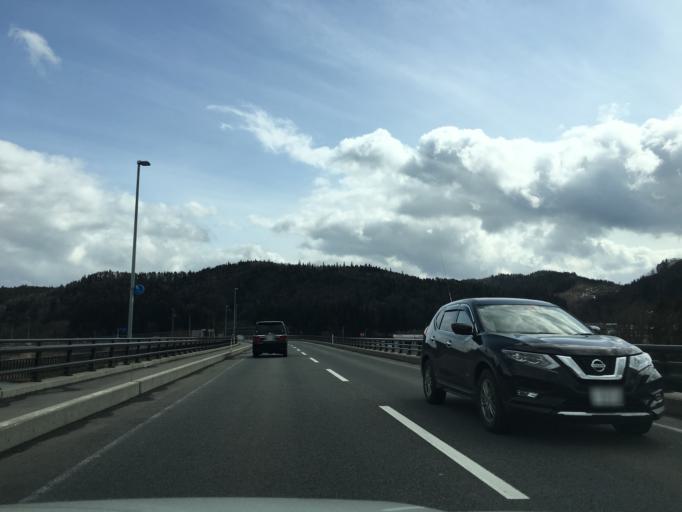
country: JP
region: Akita
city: Hanawa
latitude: 40.2256
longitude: 140.7153
